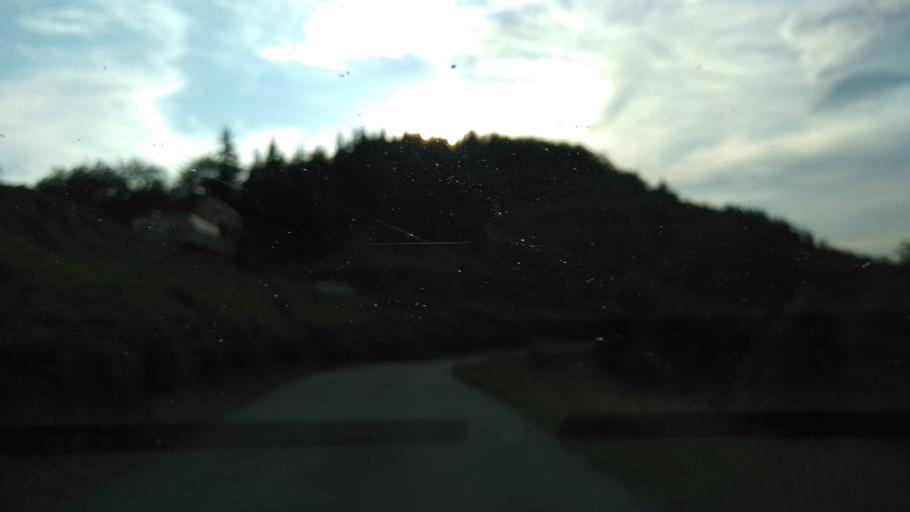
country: RO
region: Hunedoara
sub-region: Municipiul  Vulcan
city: Jiu-Paroseni
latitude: 45.3199
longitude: 23.2970
